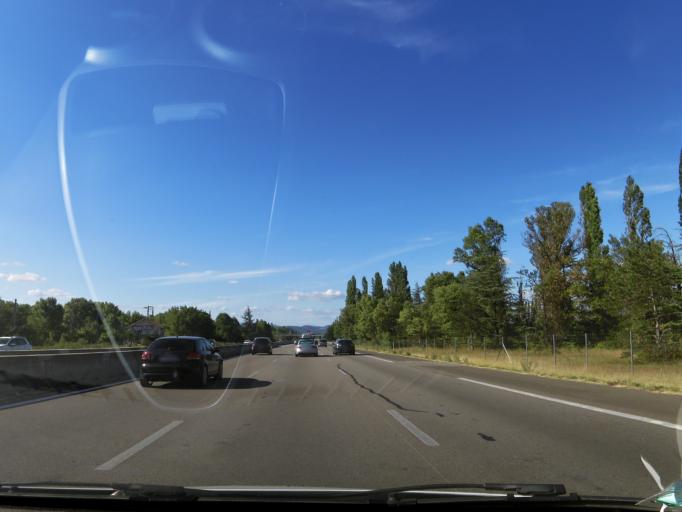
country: FR
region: Rhone-Alpes
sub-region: Departement de la Drome
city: Saulce-sur-Rhone
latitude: 44.7022
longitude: 4.7870
